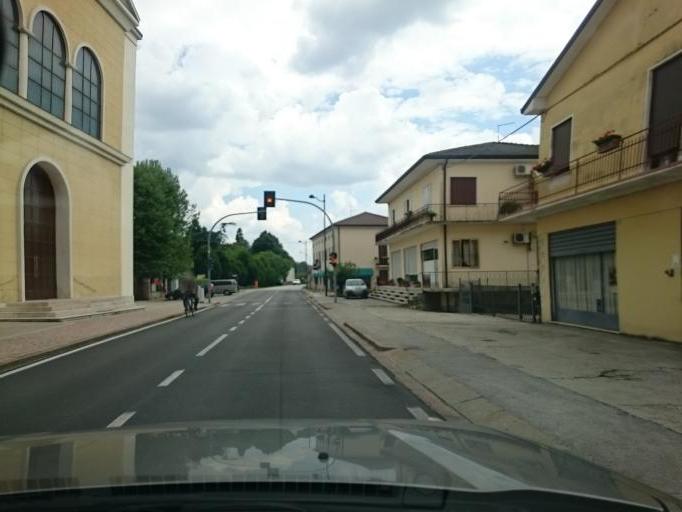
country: IT
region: Veneto
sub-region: Provincia di Vicenza
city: Longare
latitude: 45.4678
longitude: 11.6278
